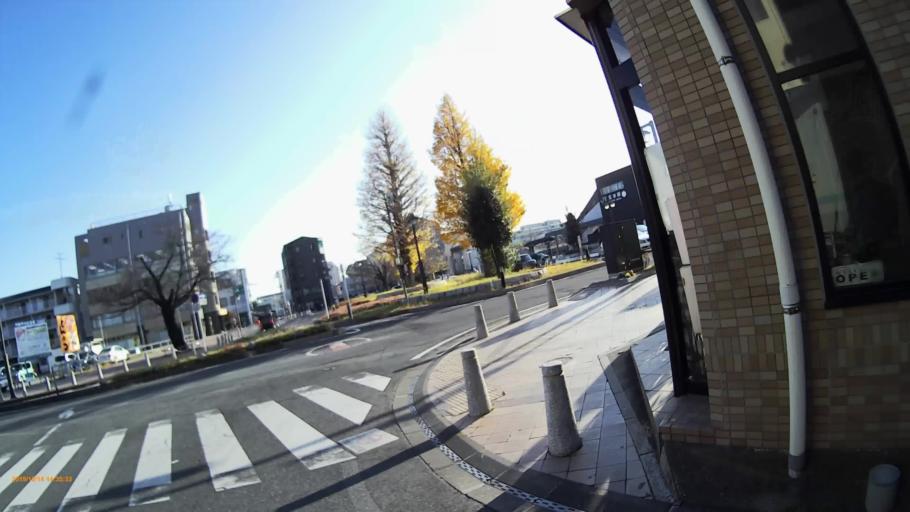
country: JP
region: Saitama
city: Okegawa
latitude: 36.0323
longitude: 139.5344
